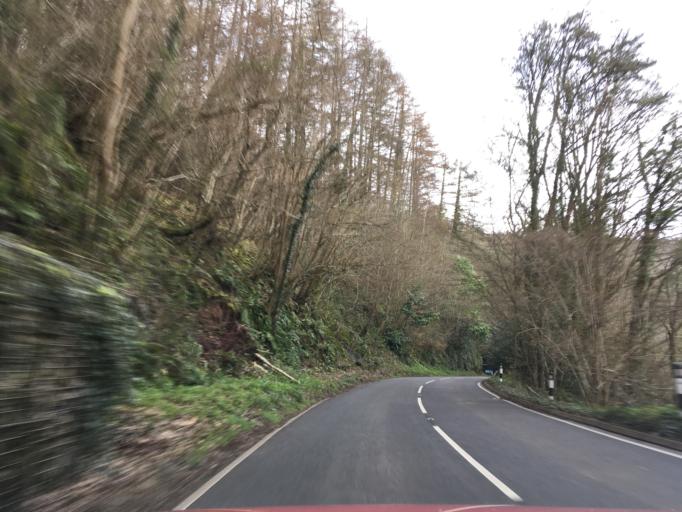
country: GB
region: Wales
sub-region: Monmouthshire
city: Tintern
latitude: 51.7283
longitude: -2.6878
